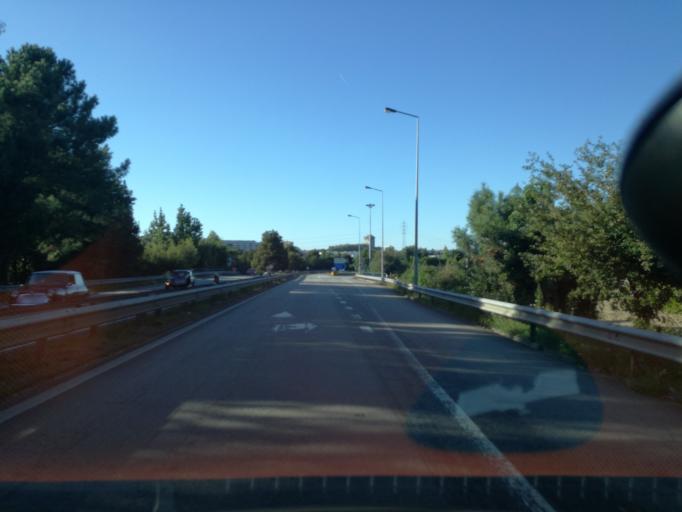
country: PT
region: Porto
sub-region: Santo Tirso
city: Sao Miguel do Couto
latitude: 41.3266
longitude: -8.4702
